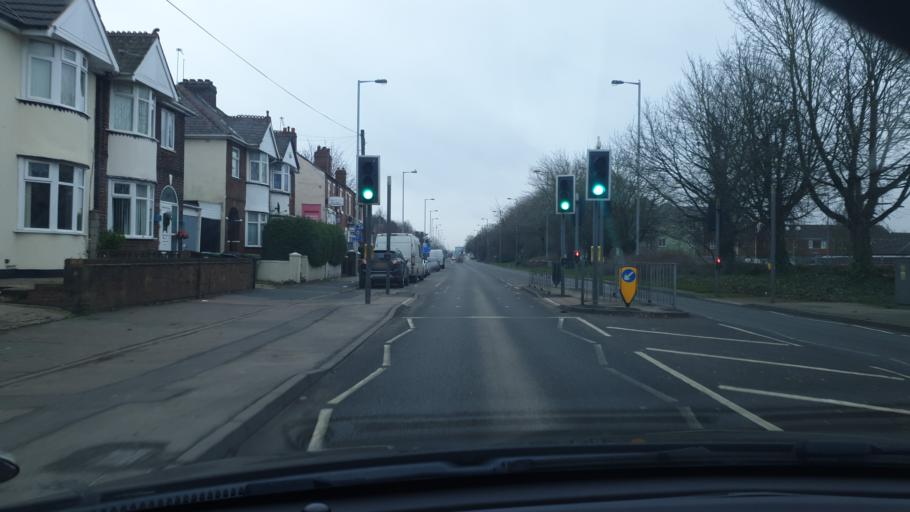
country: GB
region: England
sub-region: Wolverhampton
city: Wednesfield
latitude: 52.5835
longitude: -2.0941
